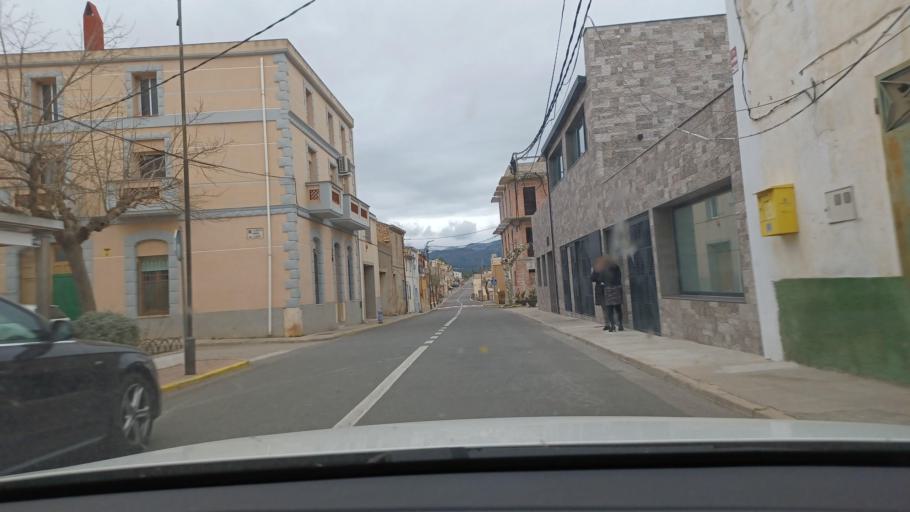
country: ES
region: Catalonia
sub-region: Provincia de Tarragona
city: Ulldecona
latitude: 40.6272
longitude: 0.3659
